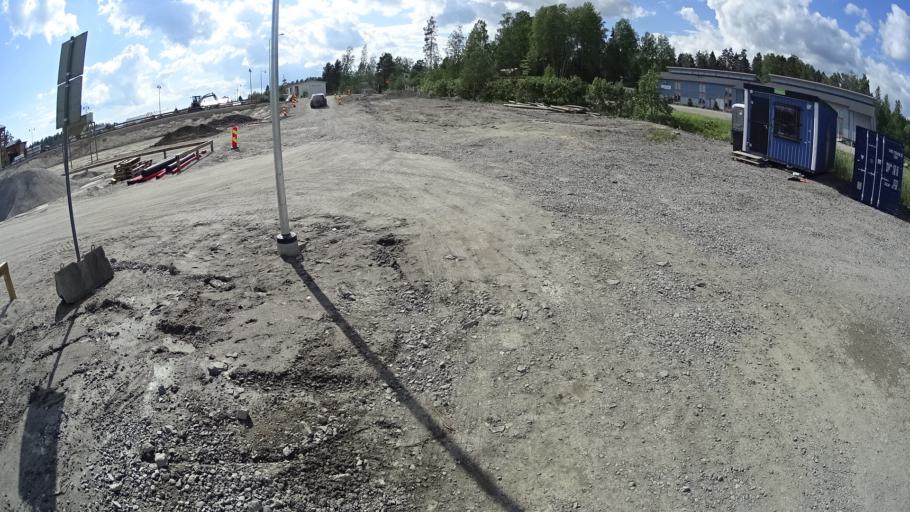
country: FI
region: Uusimaa
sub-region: Helsinki
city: Sibbo
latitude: 60.2605
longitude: 25.2366
